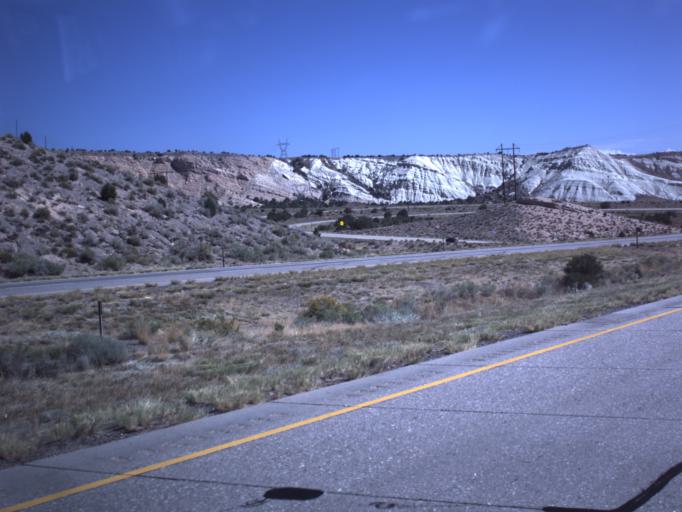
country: US
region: Utah
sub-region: Sevier County
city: Monroe
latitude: 38.5990
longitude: -112.2567
